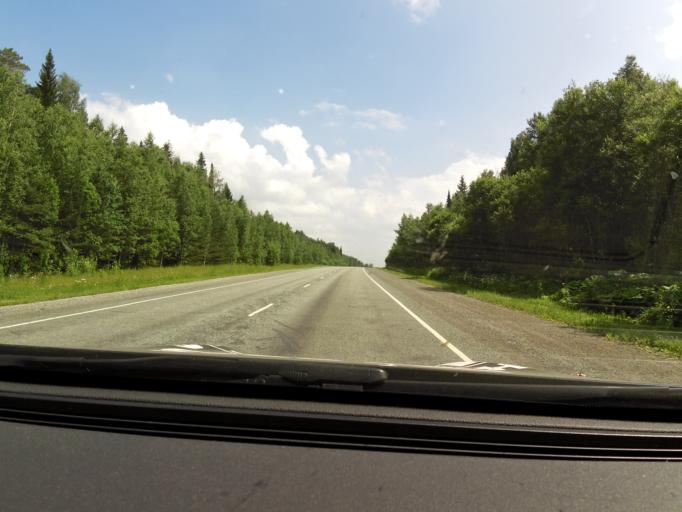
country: RU
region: Sverdlovsk
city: Achit
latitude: 56.8292
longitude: 57.7899
